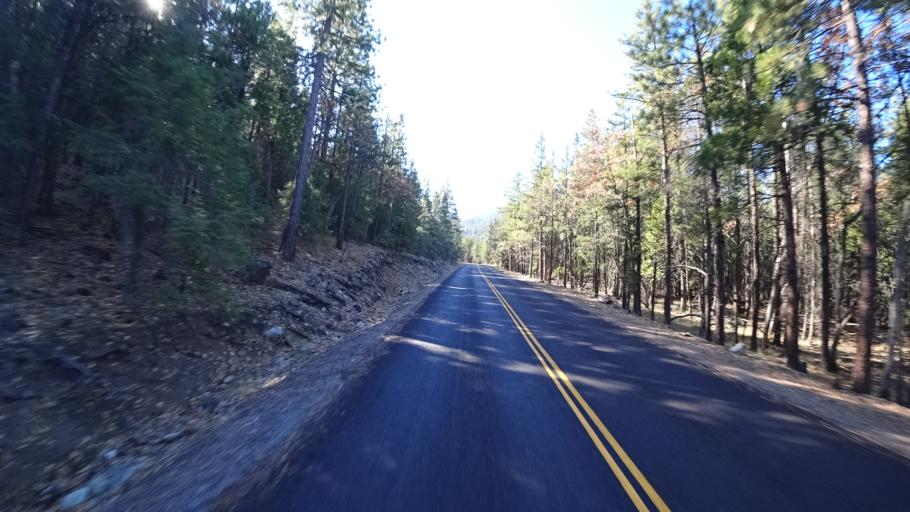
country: US
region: California
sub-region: Siskiyou County
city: Weed
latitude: 41.4315
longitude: -122.4959
